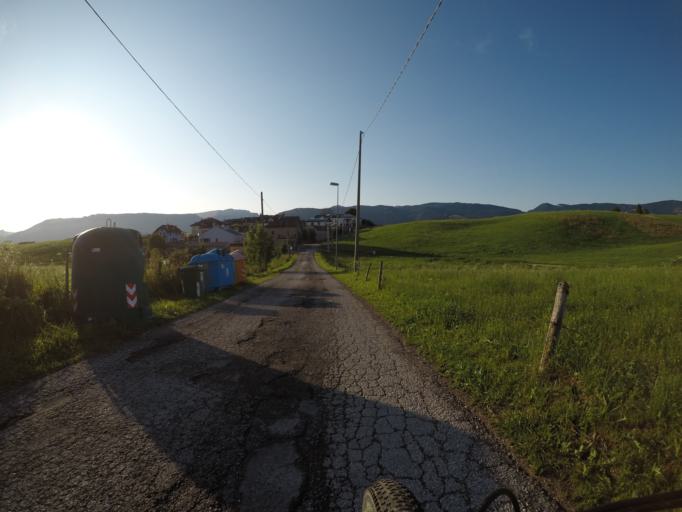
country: IT
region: Veneto
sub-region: Provincia di Vicenza
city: Asiago
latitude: 45.8631
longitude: 11.5115
